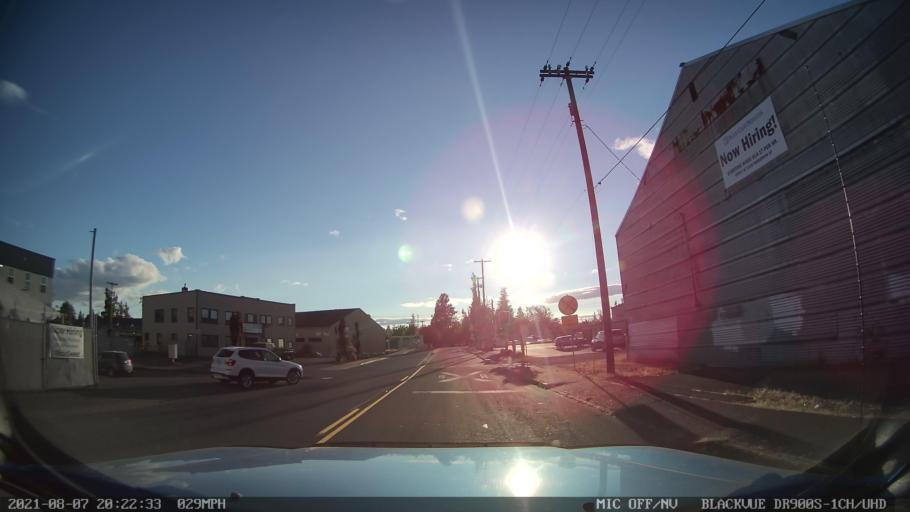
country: US
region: Oregon
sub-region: Marion County
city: Salem
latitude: 44.9564
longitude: -123.0149
